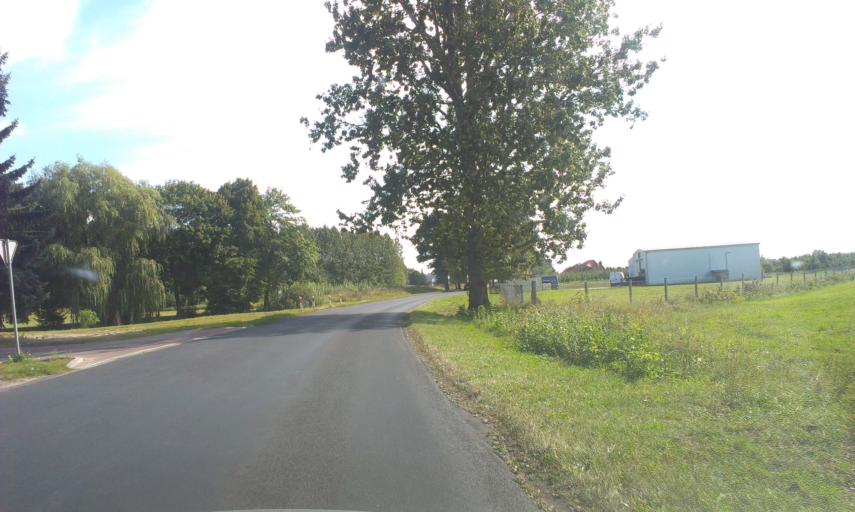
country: PL
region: Greater Poland Voivodeship
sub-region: Powiat zlotowski
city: Zlotow
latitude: 53.3494
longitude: 17.0672
